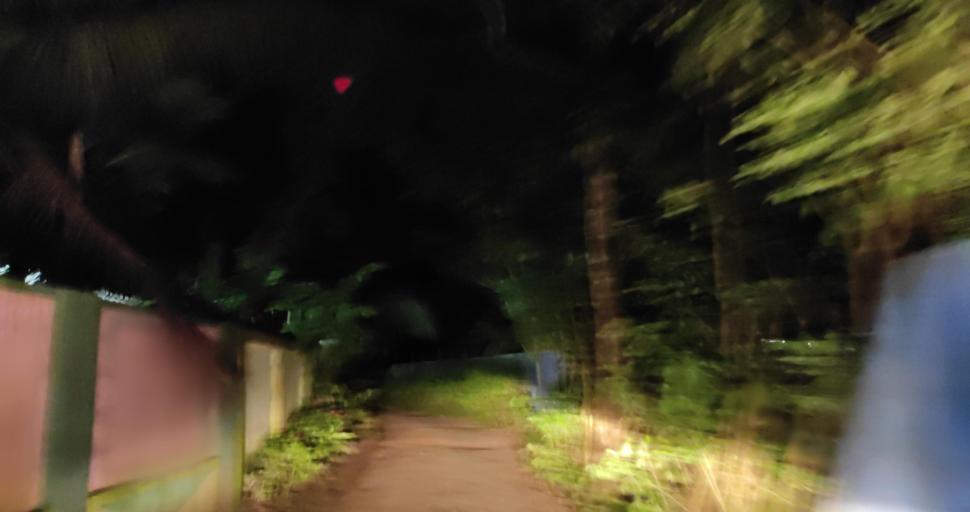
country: IN
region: Kerala
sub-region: Alappuzha
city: Vayalar
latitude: 9.6822
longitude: 76.3131
